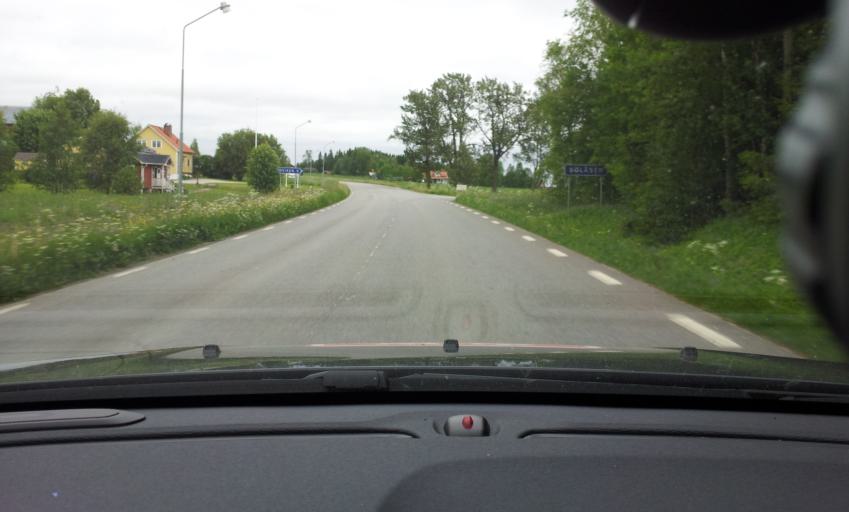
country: SE
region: Jaemtland
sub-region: Bergs Kommun
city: Hoverberg
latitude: 63.0354
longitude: 14.3454
